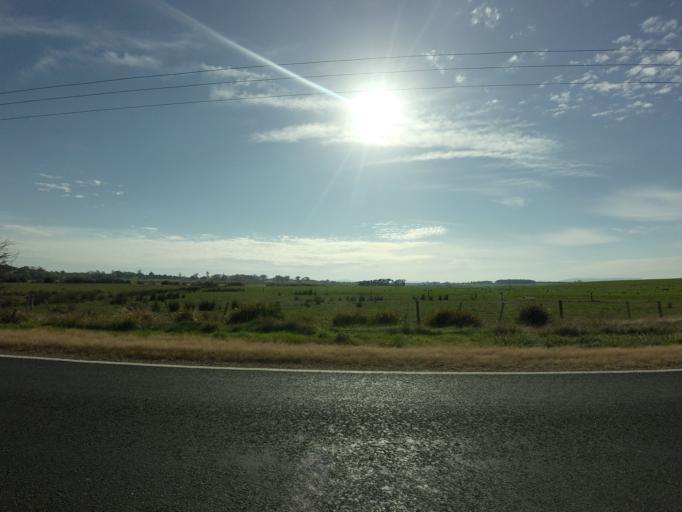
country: AU
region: Tasmania
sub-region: Meander Valley
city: Westbury
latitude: -41.5258
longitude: 146.9412
